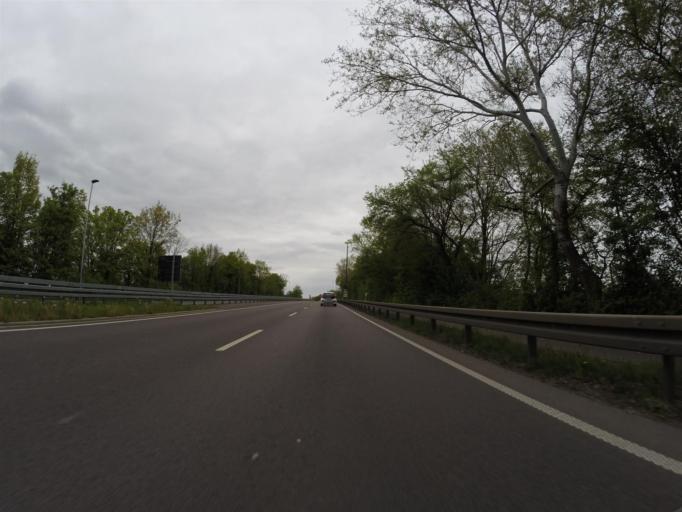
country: DE
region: Saxony-Anhalt
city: Merseburg
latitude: 51.3741
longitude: 11.9815
